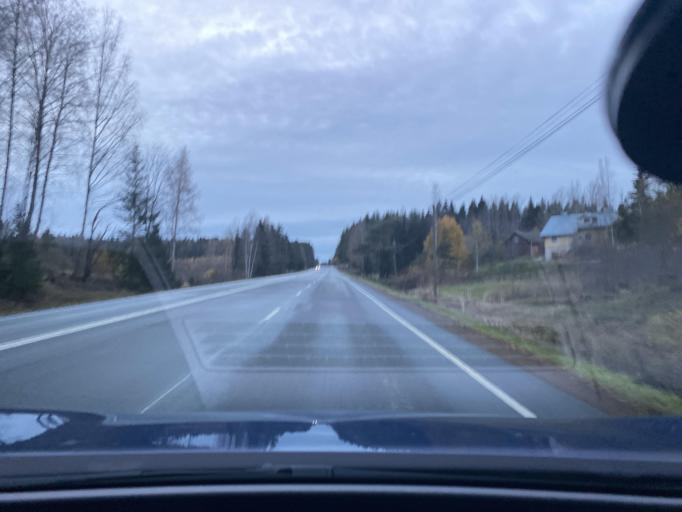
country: FI
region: Uusimaa
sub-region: Helsinki
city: Sammatti
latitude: 60.3854
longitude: 23.8687
